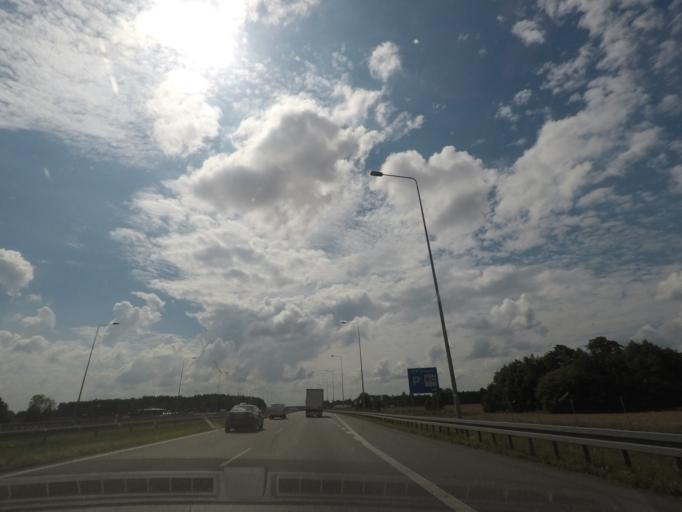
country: PL
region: Lodz Voivodeship
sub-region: Powiat leczycki
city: Piatek
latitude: 52.0101
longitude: 19.5426
